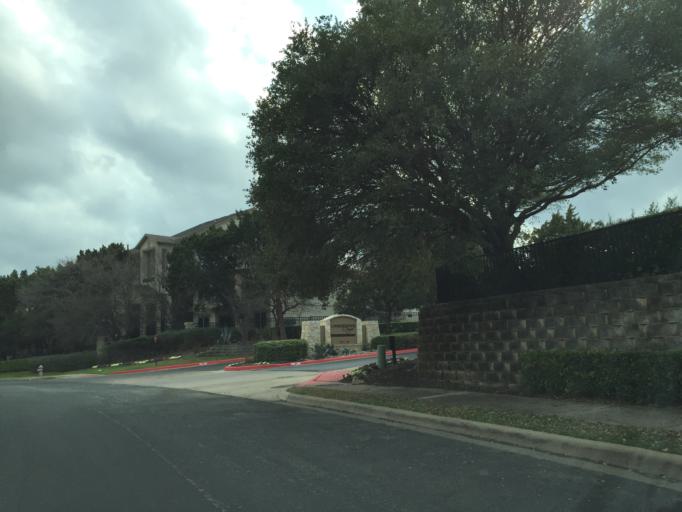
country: US
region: Texas
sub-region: Travis County
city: Wells Branch
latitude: 30.3935
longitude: -97.6767
